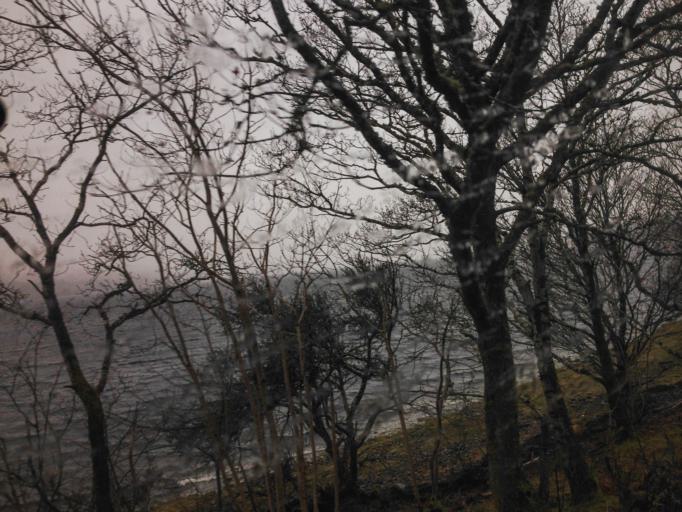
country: GB
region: Scotland
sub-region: Highland
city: Fort William
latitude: 56.8539
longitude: -5.1878
